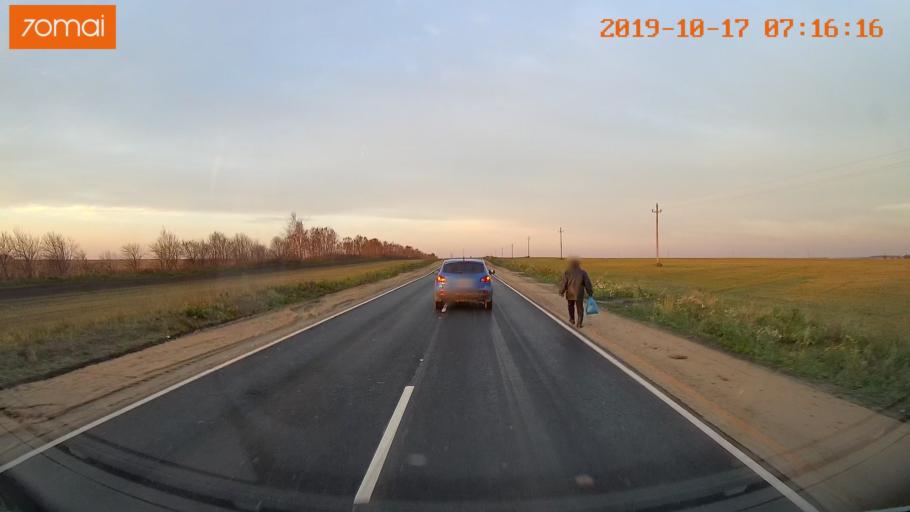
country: RU
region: Vladimir
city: Suzdal'
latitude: 56.3736
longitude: 40.2524
